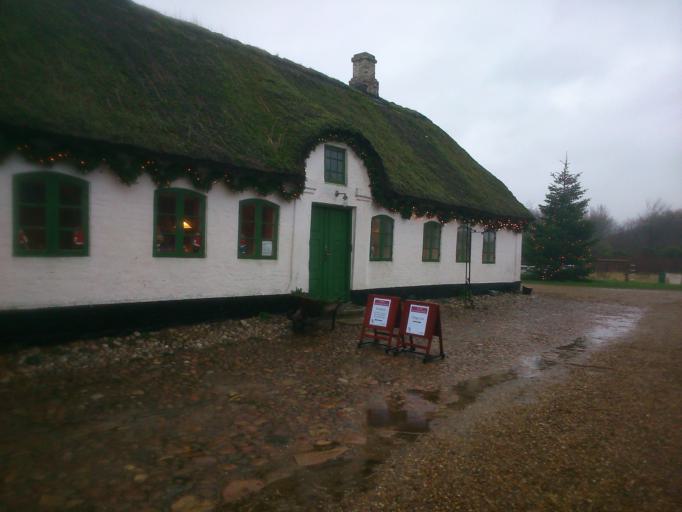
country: DK
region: Central Jutland
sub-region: Ringkobing-Skjern Kommune
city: Skjern
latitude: 56.0067
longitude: 8.4785
